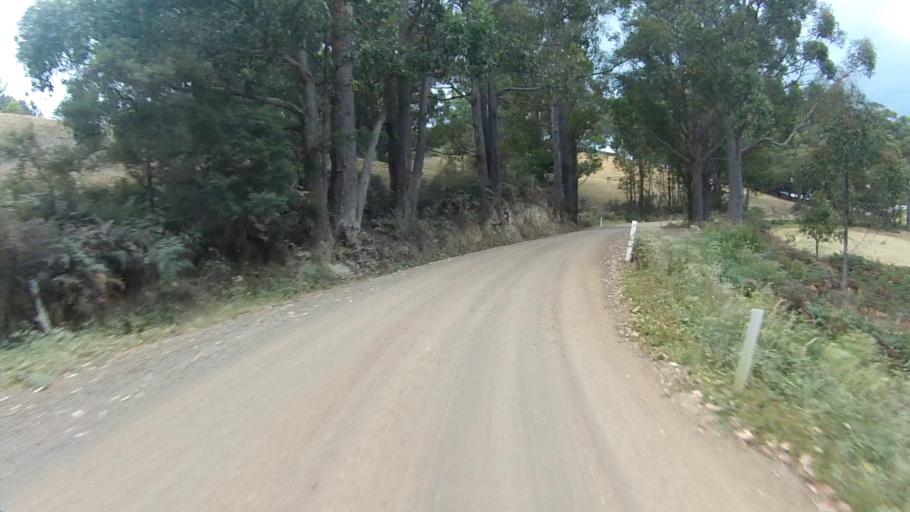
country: AU
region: Tasmania
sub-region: Huon Valley
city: Huonville
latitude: -42.9704
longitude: 147.0610
